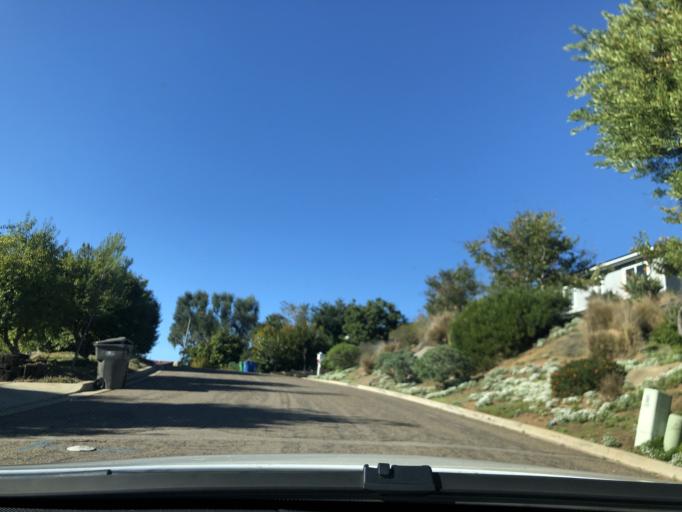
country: US
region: California
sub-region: San Diego County
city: Bostonia
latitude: 32.7817
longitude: -116.9389
